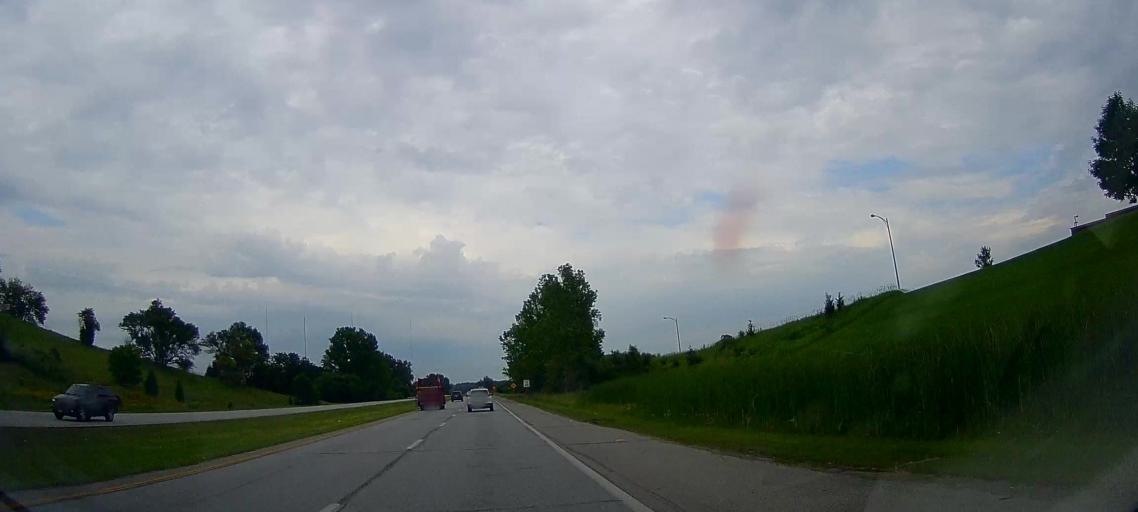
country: US
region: Nebraska
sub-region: Douglas County
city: Bennington
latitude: 41.3180
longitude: -96.0630
